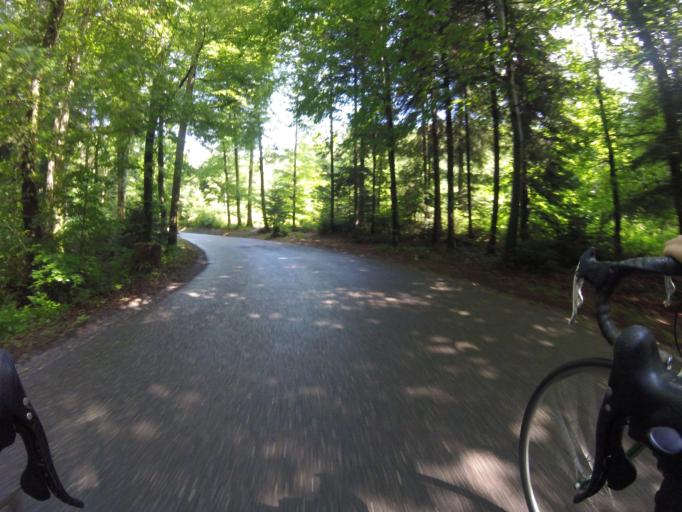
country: CH
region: Bern
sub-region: Bern-Mittelland District
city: Stettlen
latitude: 46.9387
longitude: 7.5225
